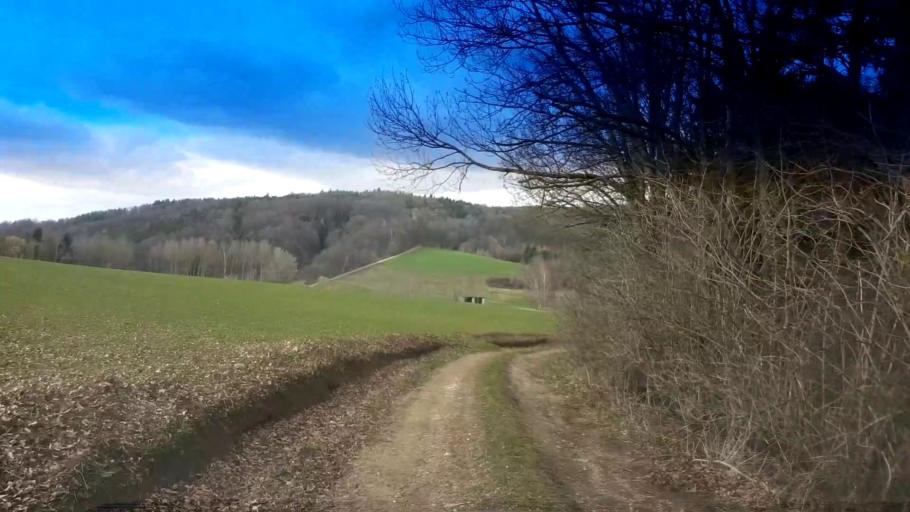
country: DE
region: Bavaria
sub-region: Upper Franconia
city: Schesslitz
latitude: 50.0064
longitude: 11.0369
